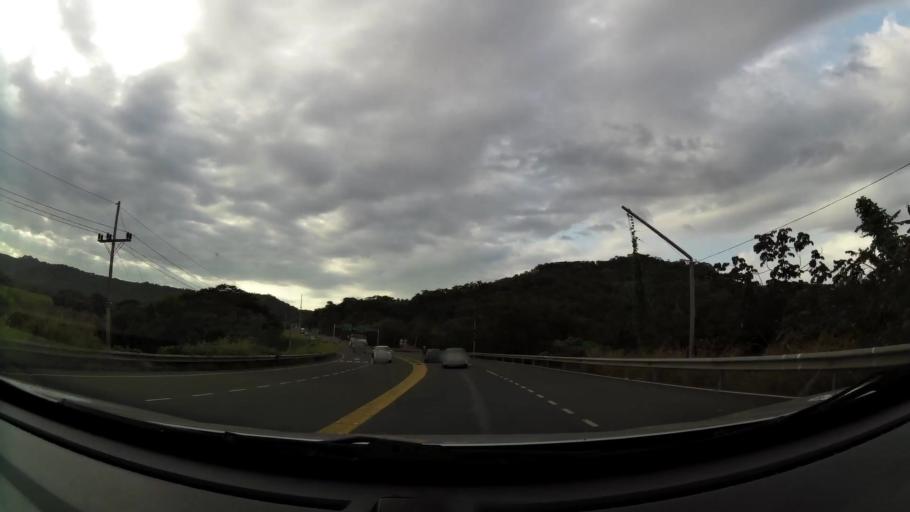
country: CR
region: Puntarenas
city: Esparza
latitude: 9.9133
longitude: -84.6731
